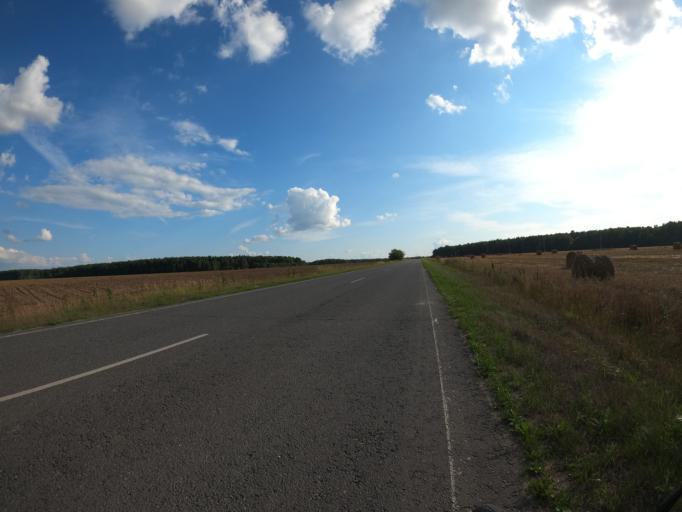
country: RU
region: Moskovskaya
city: Meshcherino
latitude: 55.1755
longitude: 38.4689
